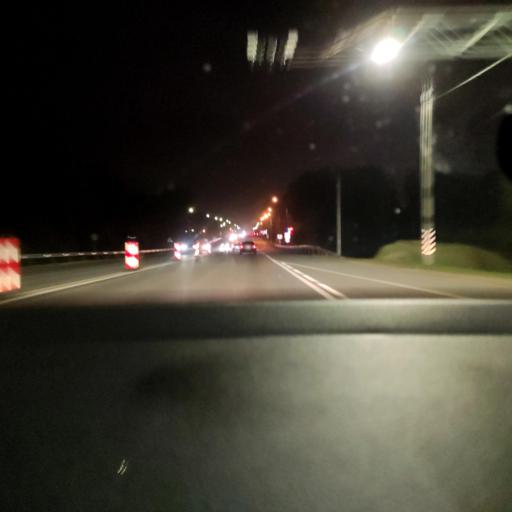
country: RU
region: Moskovskaya
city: Ateptsevo
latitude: 55.2745
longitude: 36.6941
